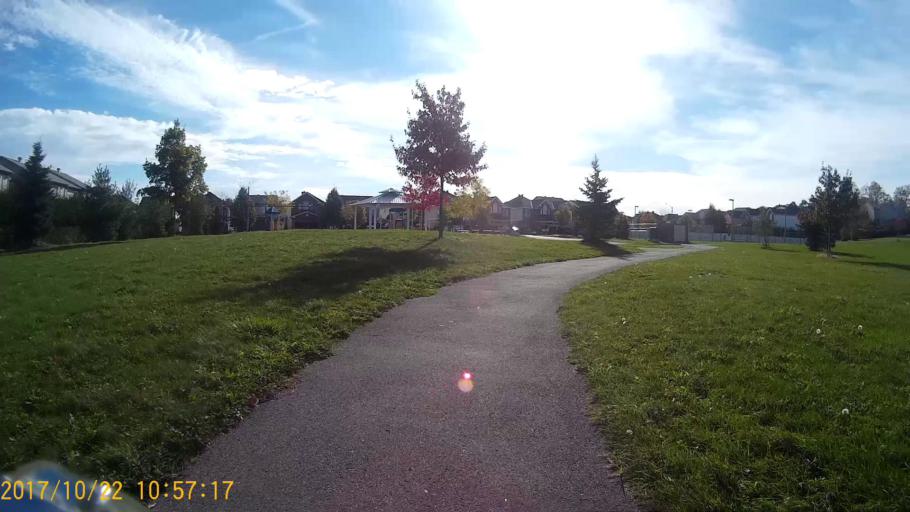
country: CA
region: Ontario
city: Bells Corners
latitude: 45.3572
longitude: -75.9260
